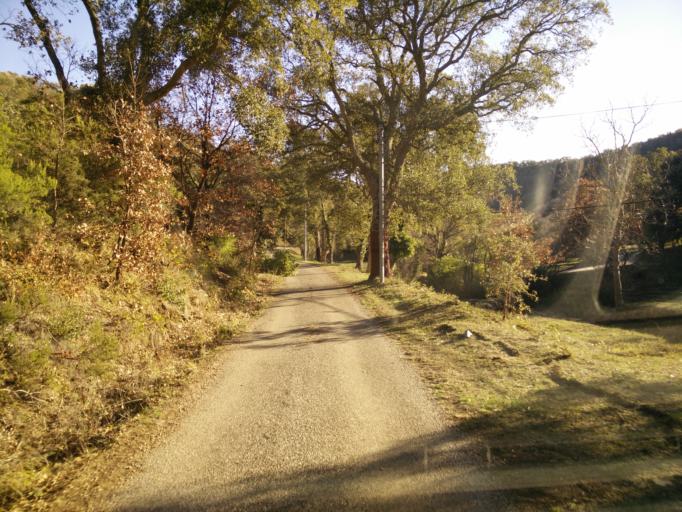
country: FR
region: Provence-Alpes-Cote d'Azur
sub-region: Departement du Var
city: Collobrieres
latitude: 43.2525
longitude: 6.3094
